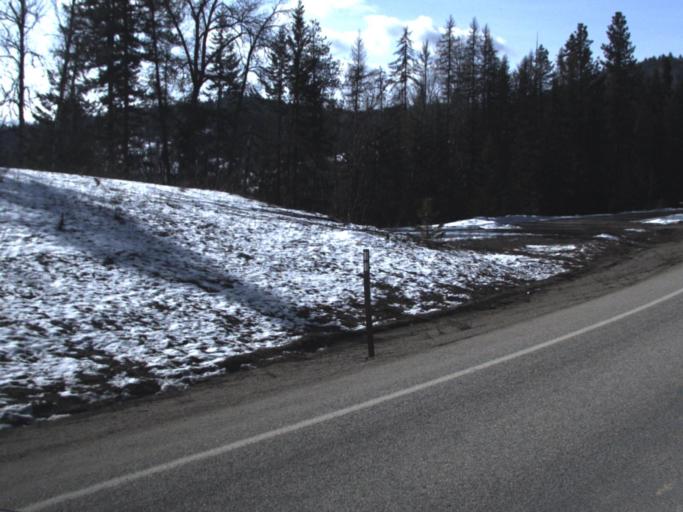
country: CA
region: British Columbia
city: Fruitvale
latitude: 48.6826
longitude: -117.4323
